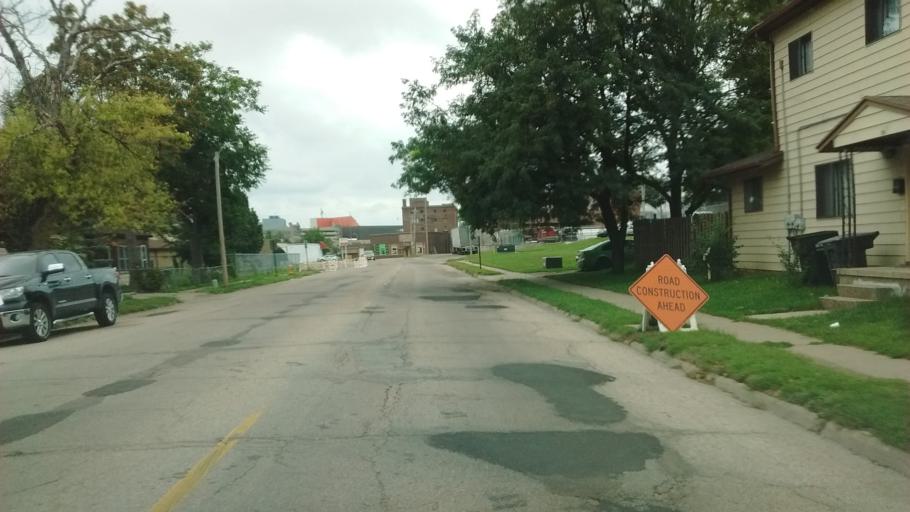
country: US
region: Iowa
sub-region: Woodbury County
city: Sioux City
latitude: 42.4973
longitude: -96.4143
